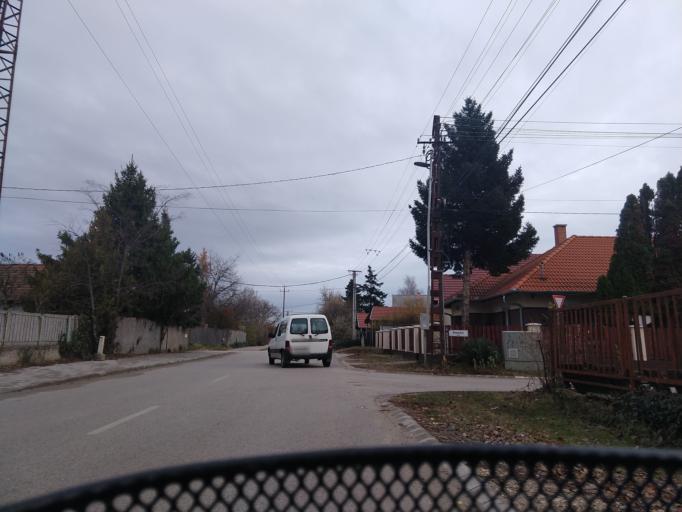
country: HU
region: Pest
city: Veresegyhaz
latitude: 47.6483
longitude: 19.2741
